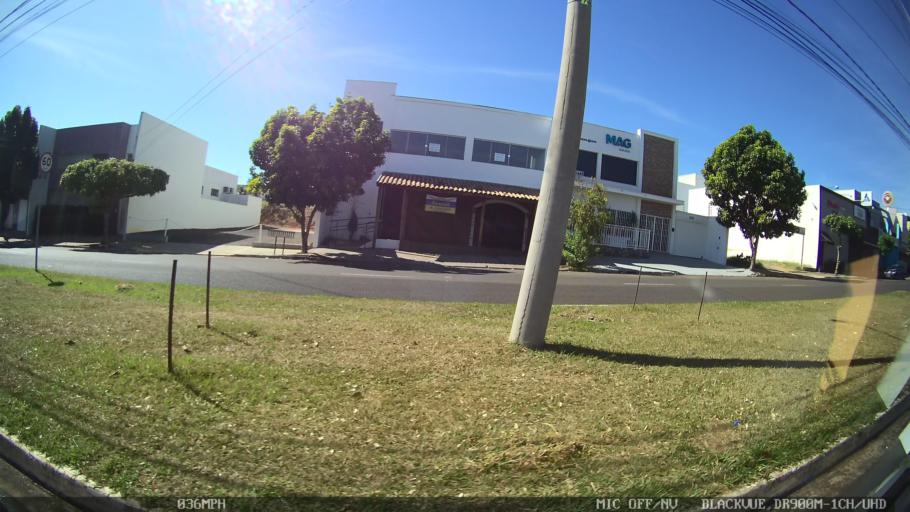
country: BR
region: Sao Paulo
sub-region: Franca
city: Franca
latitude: -20.5397
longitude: -47.3756
